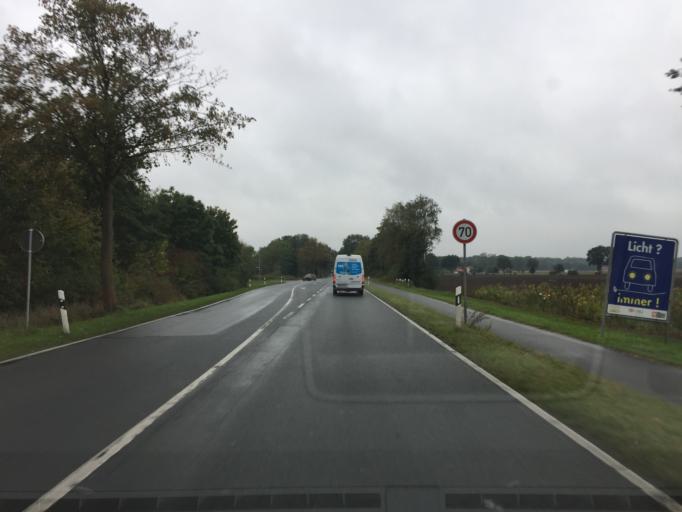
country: DE
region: Lower Saxony
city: Nienburg
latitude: 52.6183
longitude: 9.1964
